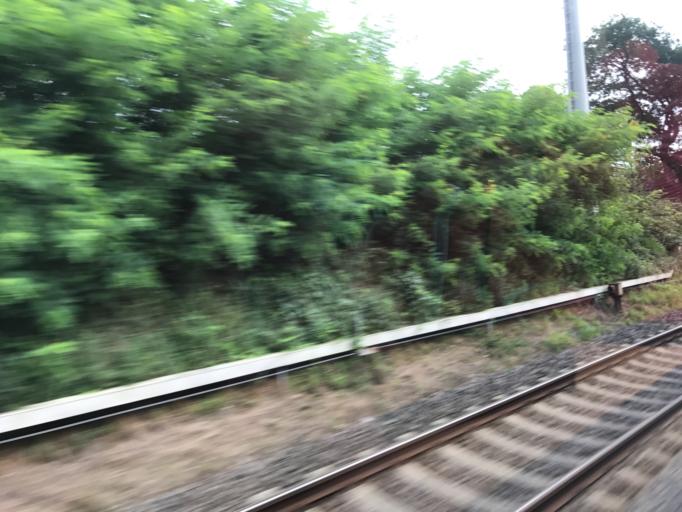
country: DE
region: Hesse
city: Leun
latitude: 50.5475
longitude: 8.3384
